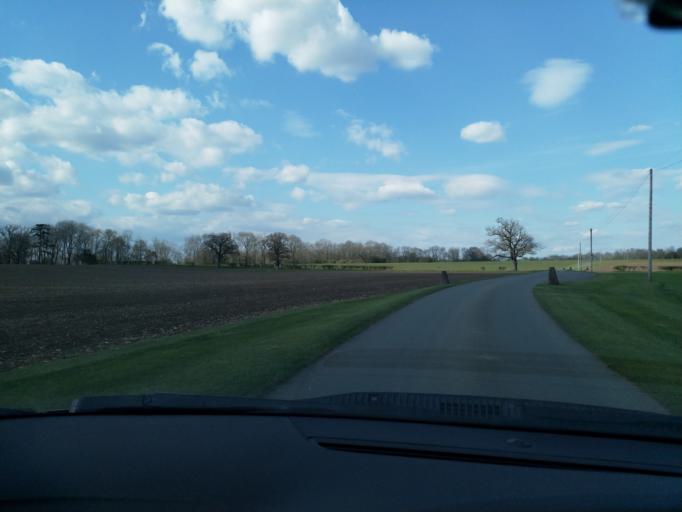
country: GB
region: England
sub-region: Warwickshire
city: Wellesbourne Mountford
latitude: 52.1717
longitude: -1.5714
